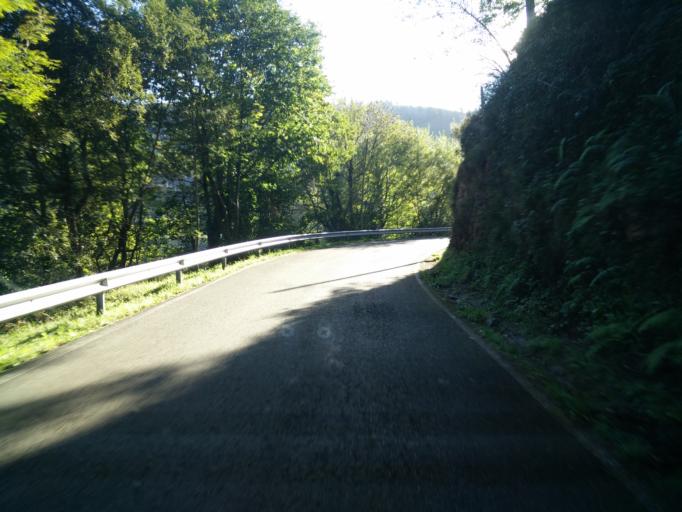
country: ES
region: Cantabria
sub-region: Provincia de Cantabria
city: San Pedro del Romeral
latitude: 43.1339
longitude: -3.8150
